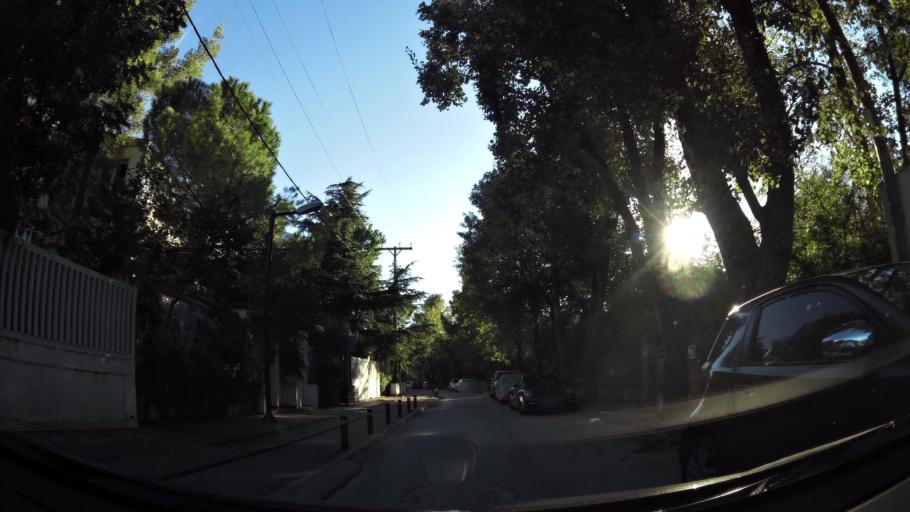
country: GR
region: Attica
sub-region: Nomarchia Athinas
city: Nea Erythraia
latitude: 38.0971
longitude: 23.8274
